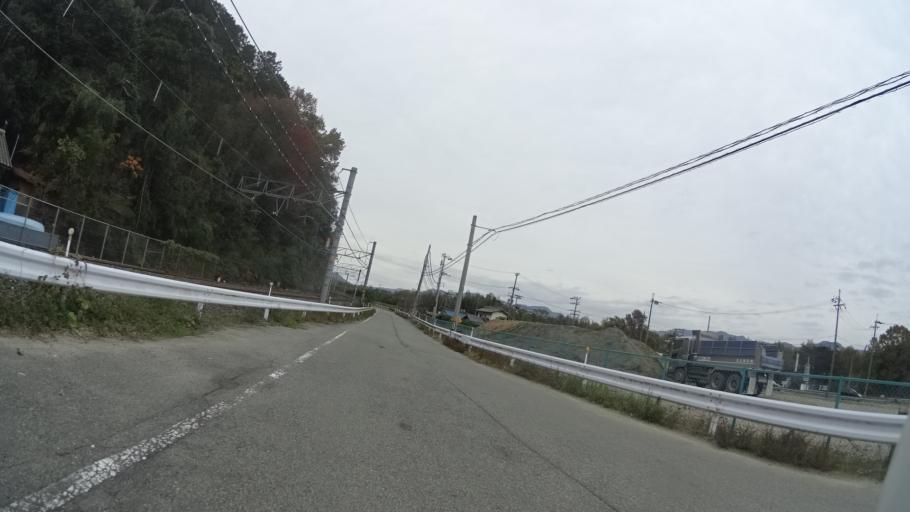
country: JP
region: Kyoto
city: Kameoka
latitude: 35.0603
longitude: 135.5454
